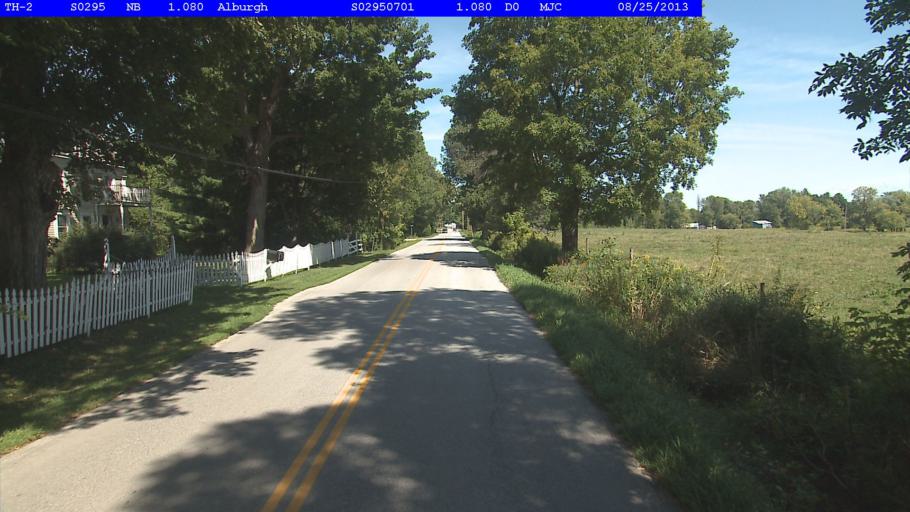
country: US
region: Vermont
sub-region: Franklin County
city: Swanton
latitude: 44.9891
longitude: -73.2243
